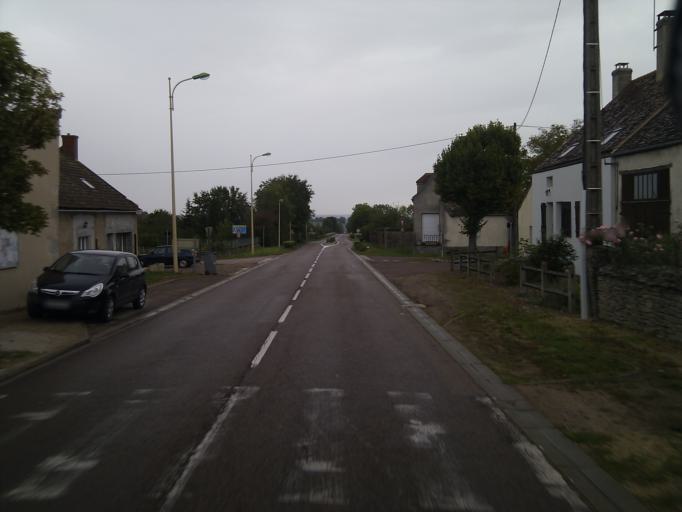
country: FR
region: Bourgogne
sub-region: Departement de la Cote-d'Or
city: Saulieu
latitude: 47.3523
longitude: 4.2816
